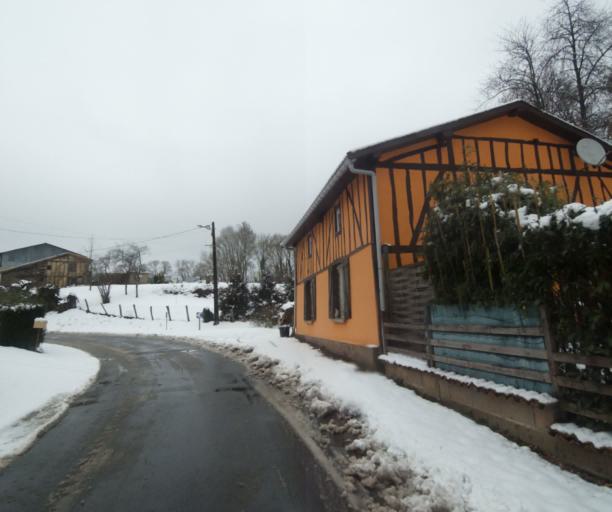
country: FR
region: Champagne-Ardenne
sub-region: Departement de la Haute-Marne
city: Laneuville-a-Remy
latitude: 48.4606
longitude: 4.9200
